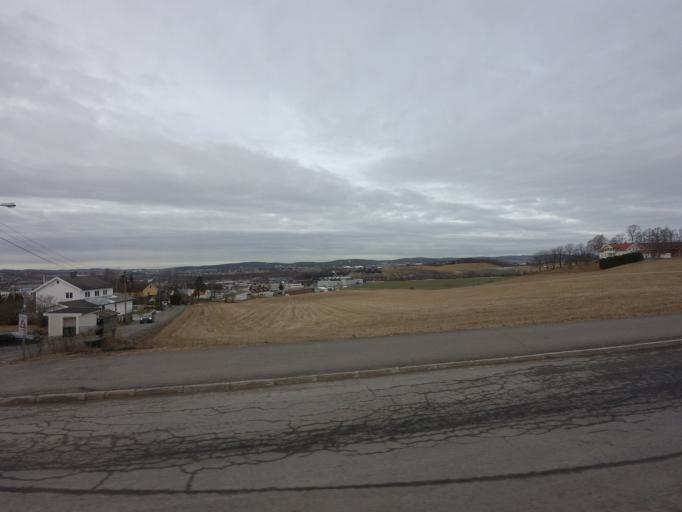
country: NO
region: Akershus
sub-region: Skedsmo
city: Lillestrom
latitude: 59.9778
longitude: 11.0561
